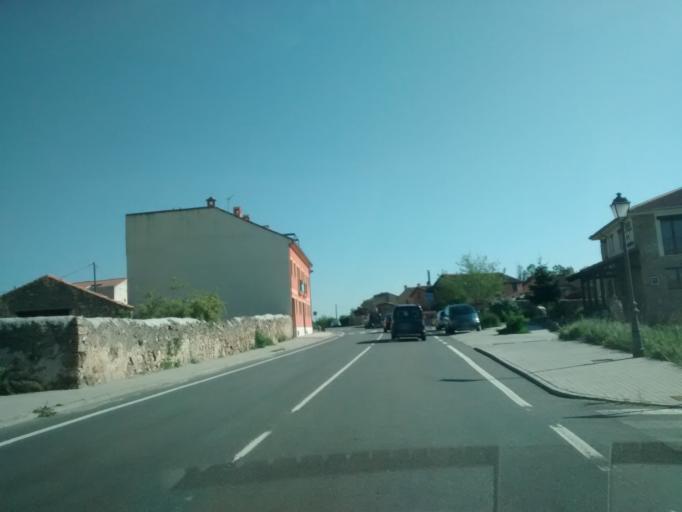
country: ES
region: Castille and Leon
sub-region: Provincia de Segovia
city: Torrecaballeros
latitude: 40.9910
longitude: -4.0234
